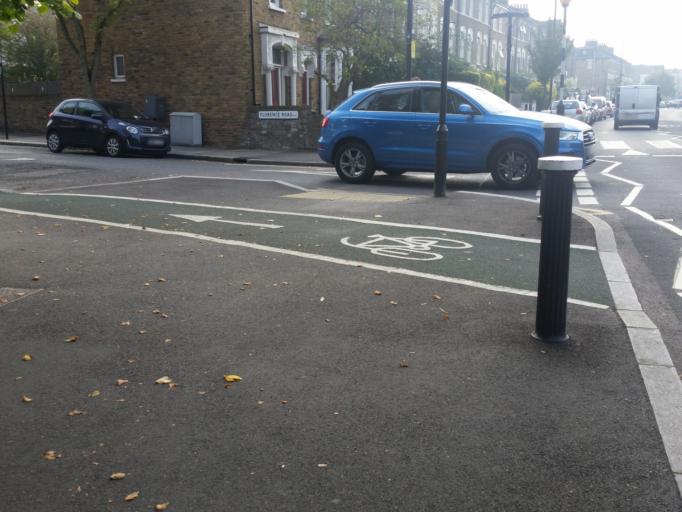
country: GB
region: England
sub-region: Greater London
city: Harringay
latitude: 51.5707
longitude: -0.1080
